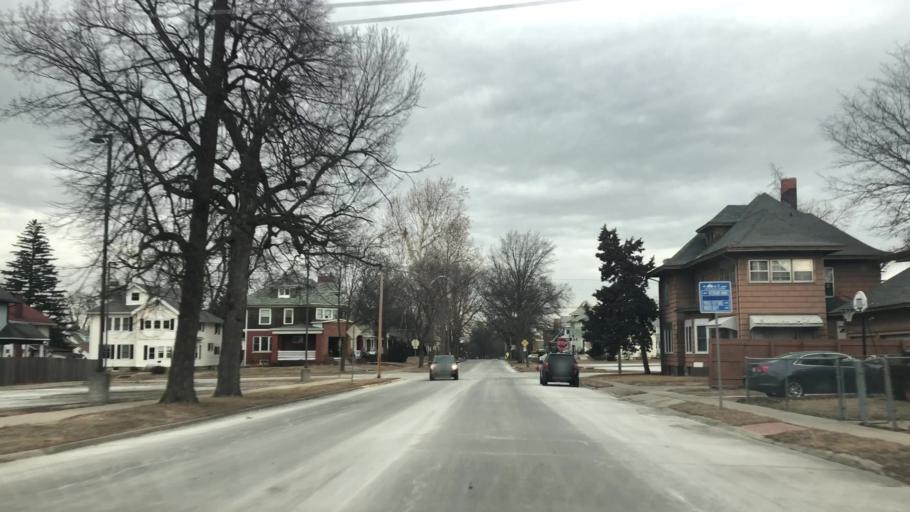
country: US
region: Iowa
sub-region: Marshall County
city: Marshalltown
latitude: 42.0497
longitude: -92.9179
